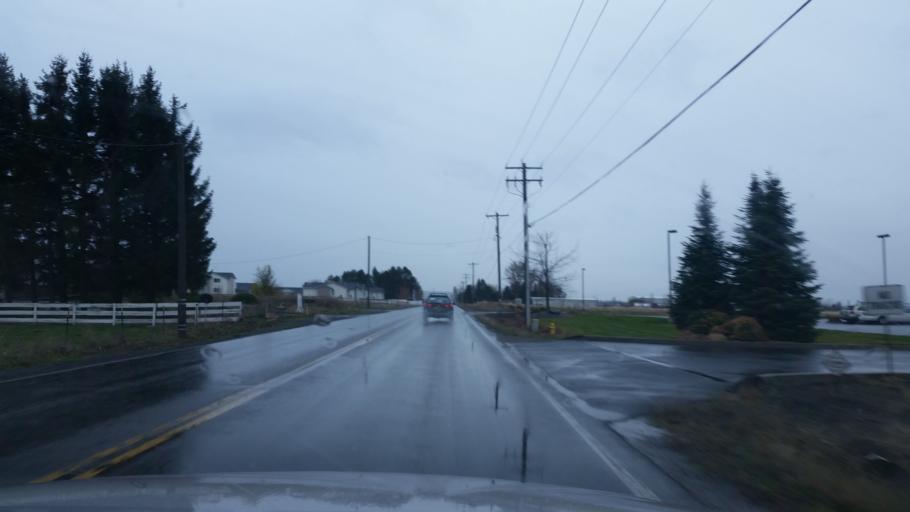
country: US
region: Washington
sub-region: Spokane County
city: Airway Heights
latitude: 47.6410
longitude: -117.5609
